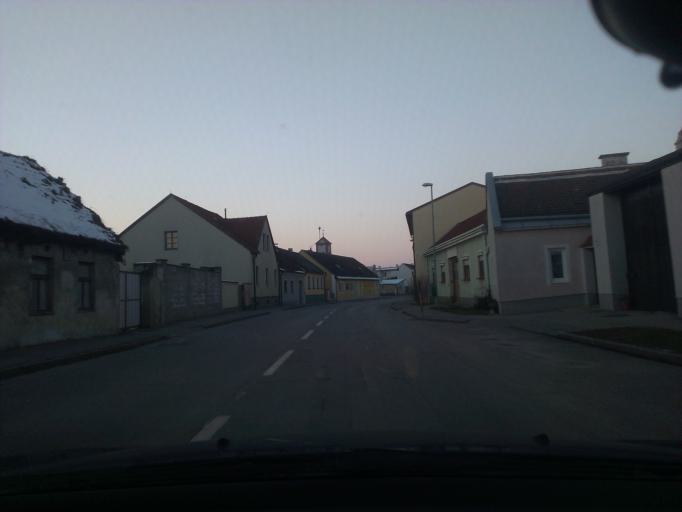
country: AT
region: Lower Austria
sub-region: Politischer Bezirk Bruck an der Leitha
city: Enzersdorf an der Fischa
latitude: 48.0802
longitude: 16.6069
